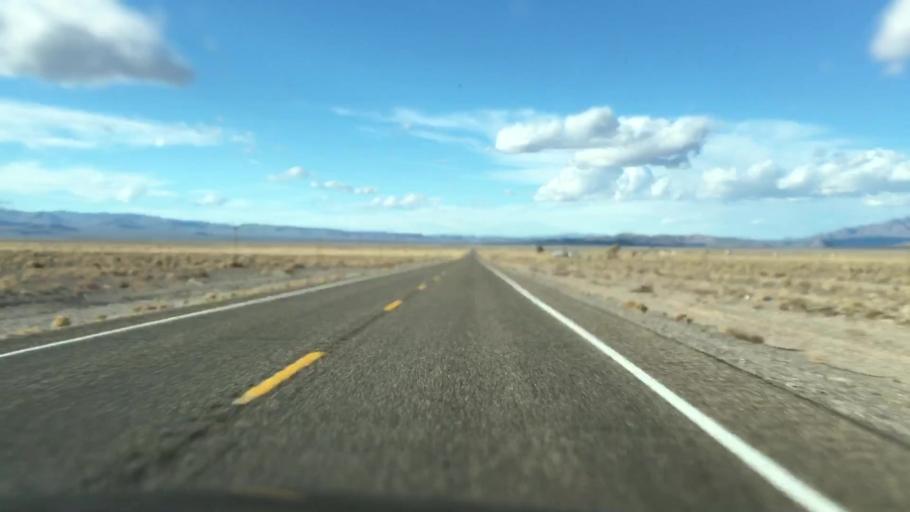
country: US
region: Nevada
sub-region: Nye County
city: Beatty
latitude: 37.2452
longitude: -116.9987
